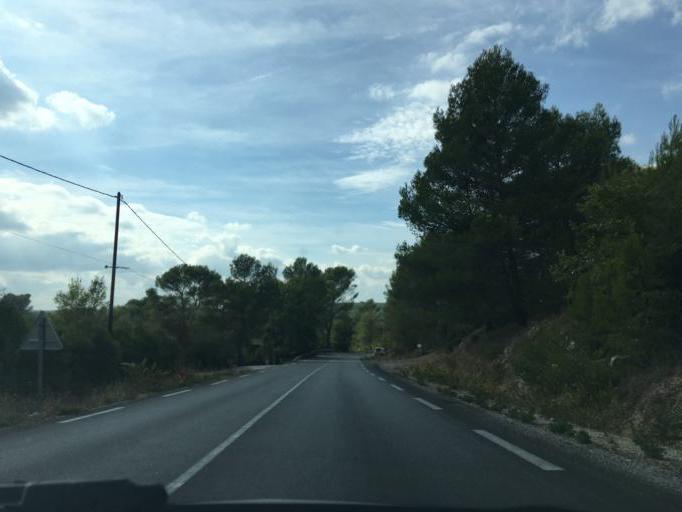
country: FR
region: Provence-Alpes-Cote d'Azur
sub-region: Departement du Var
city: Flayosc
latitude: 43.5416
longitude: 6.3650
